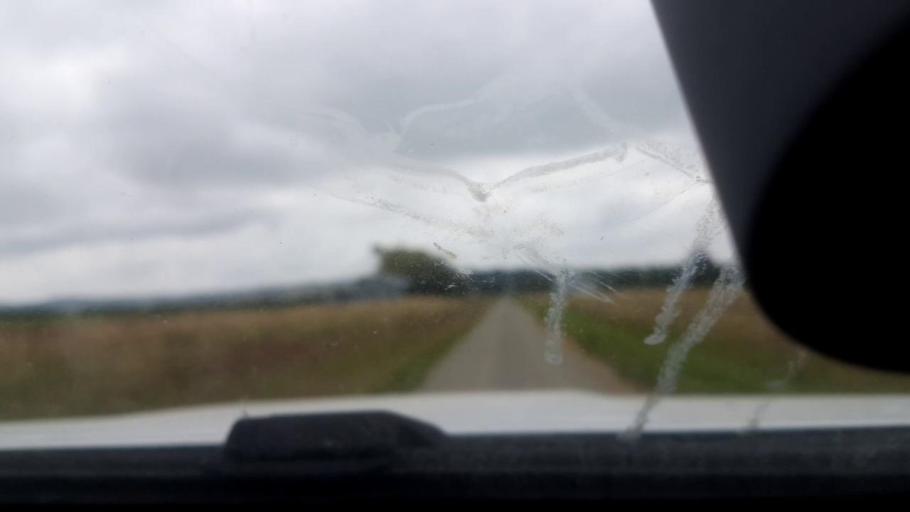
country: NZ
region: Canterbury
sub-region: Timaru District
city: Pleasant Point
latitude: -44.2271
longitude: 171.1650
